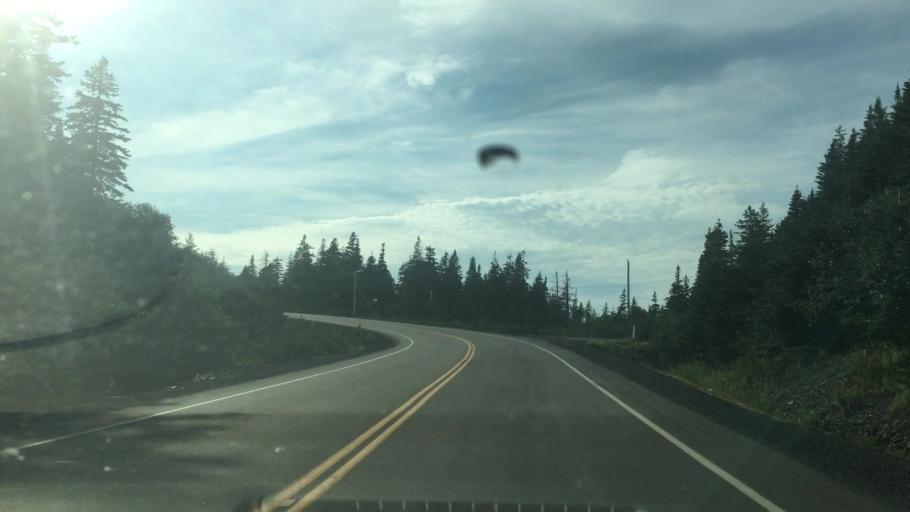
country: CA
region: Nova Scotia
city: Sydney Mines
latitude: 46.8240
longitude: -60.6577
